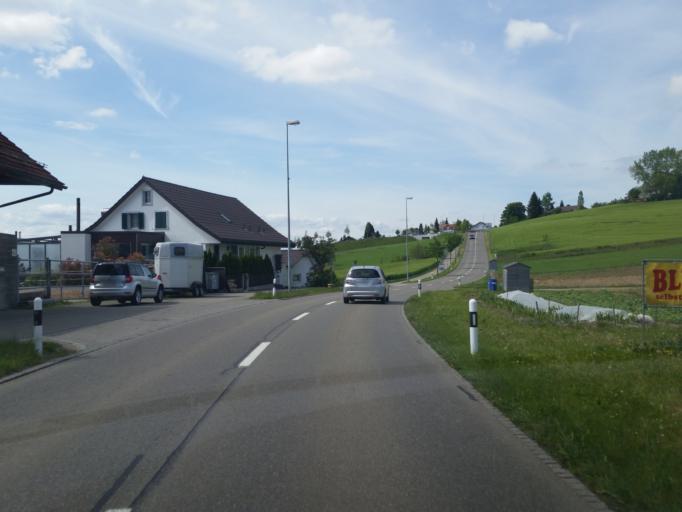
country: CH
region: Aargau
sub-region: Bezirk Bremgarten
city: Berikon
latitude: 47.3401
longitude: 8.3825
